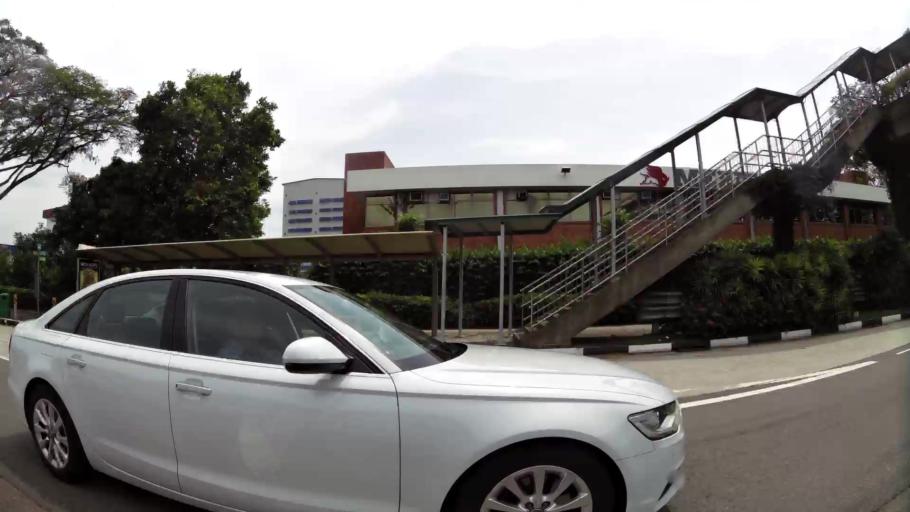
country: MY
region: Johor
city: Johor Bahru
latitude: 1.3219
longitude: 103.6708
